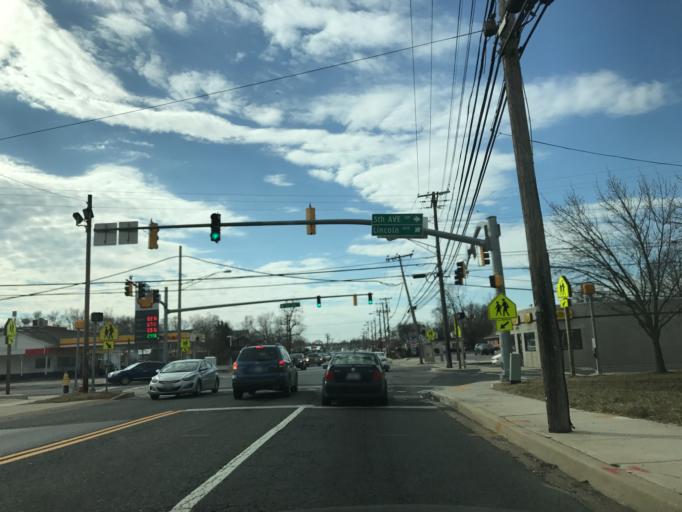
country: US
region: Maryland
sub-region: Anne Arundel County
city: Glen Burnie
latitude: 39.1581
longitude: -76.6289
